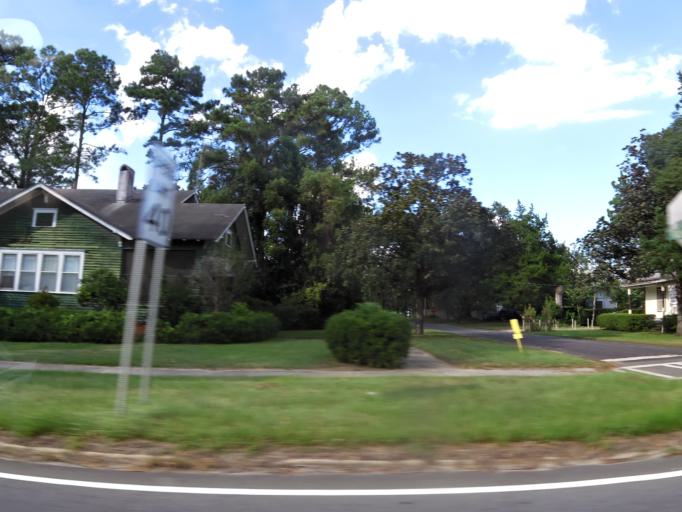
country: US
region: Georgia
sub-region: Brooks County
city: Quitman
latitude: 30.7852
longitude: -83.5654
